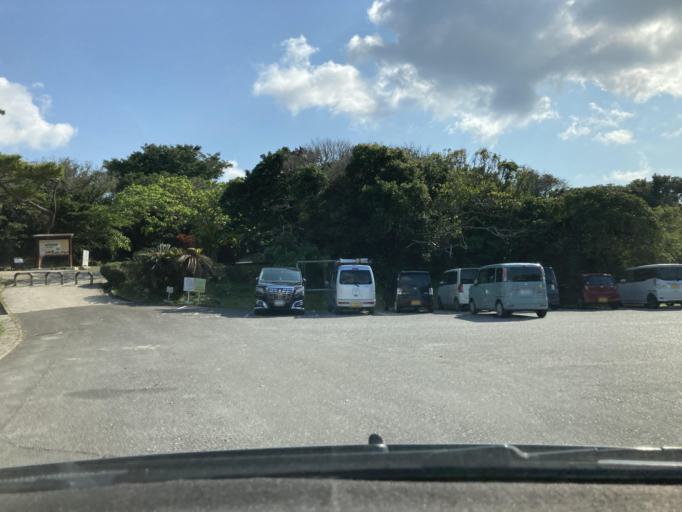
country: JP
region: Okinawa
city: Ginowan
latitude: 26.2482
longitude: 127.7302
